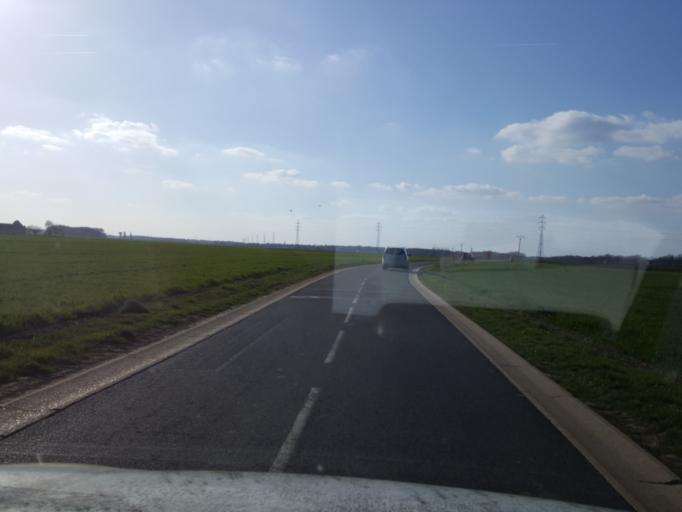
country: FR
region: Ile-de-France
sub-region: Departement des Yvelines
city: Gazeran
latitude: 48.6241
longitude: 1.8034
